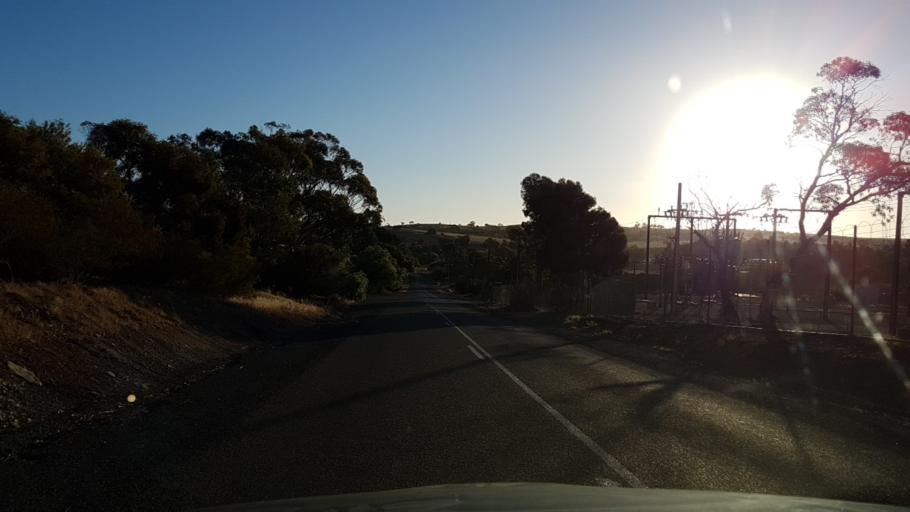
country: AU
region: South Australia
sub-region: Clare and Gilbert Valleys
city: Clare
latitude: -34.0223
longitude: 138.6920
